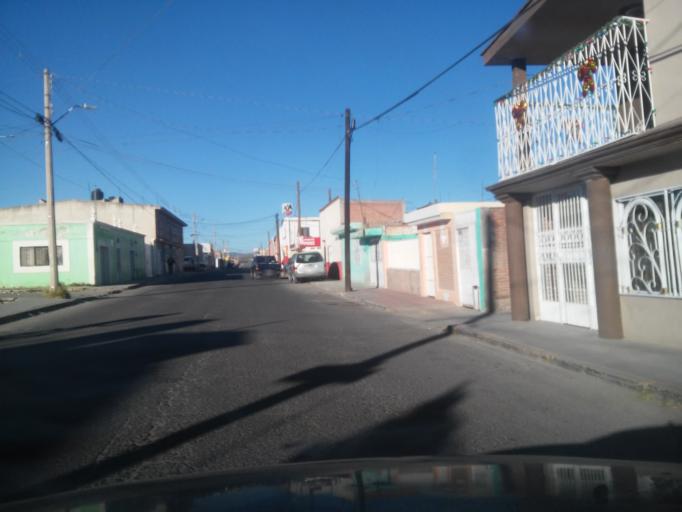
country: MX
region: Durango
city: Victoria de Durango
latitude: 24.0135
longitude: -104.6485
